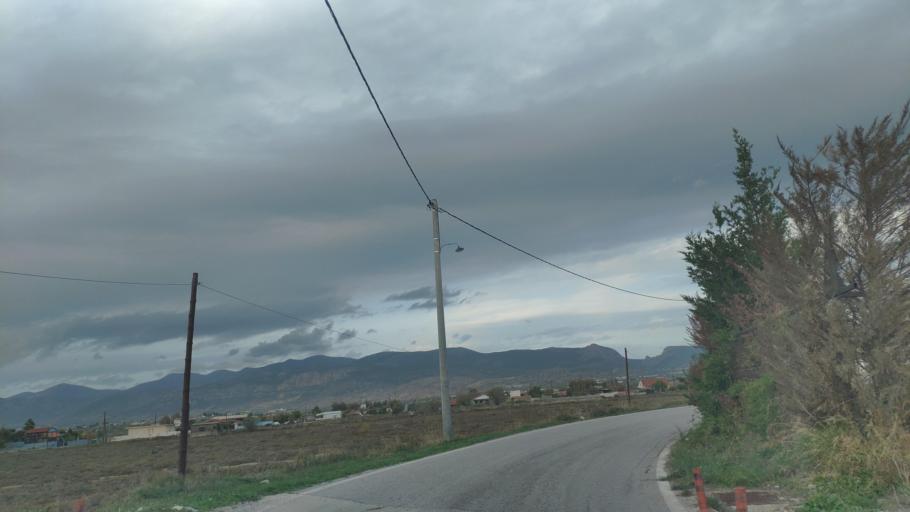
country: GR
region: Attica
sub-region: Nomarchia Dytikis Attikis
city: Megara
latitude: 37.9812
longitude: 23.3834
